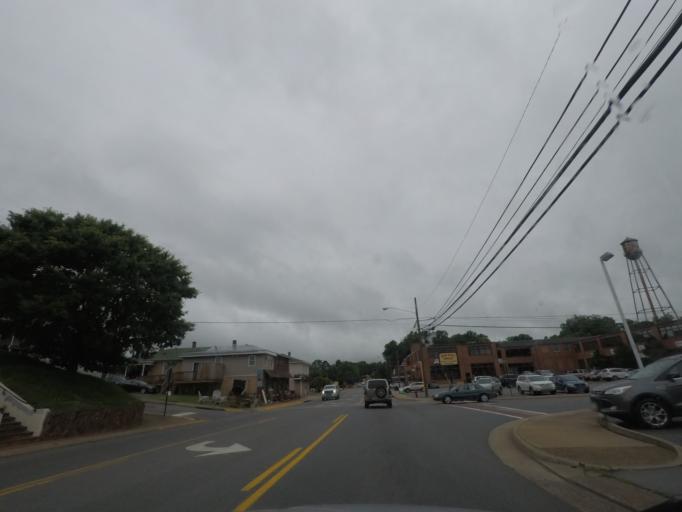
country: US
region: Virginia
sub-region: Orange County
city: Orange
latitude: 38.2509
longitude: -78.1137
